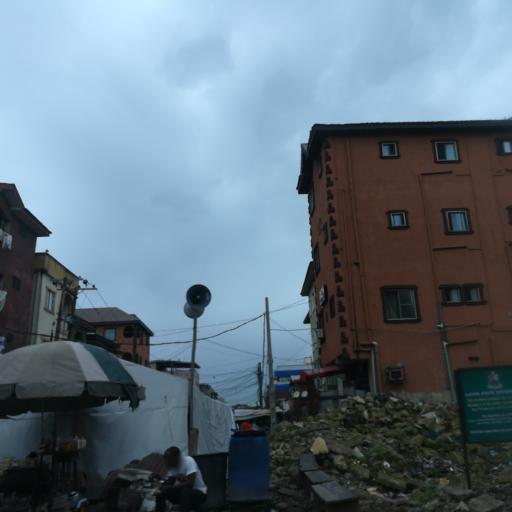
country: NG
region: Lagos
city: Ebute Metta
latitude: 6.4880
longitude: 3.3836
